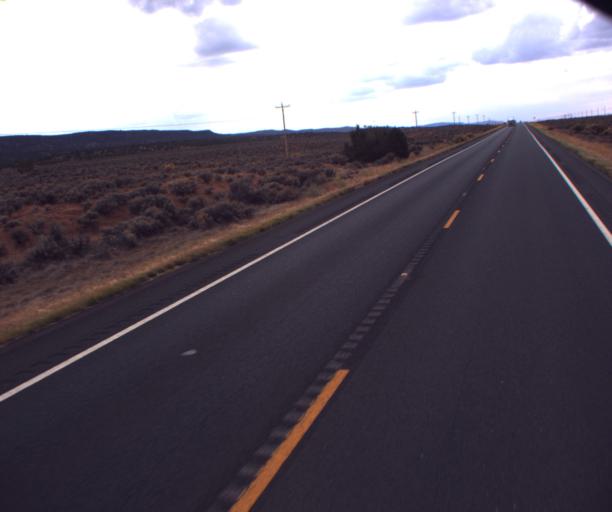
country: US
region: Arizona
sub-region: Navajo County
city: Kayenta
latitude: 36.5327
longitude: -110.5640
